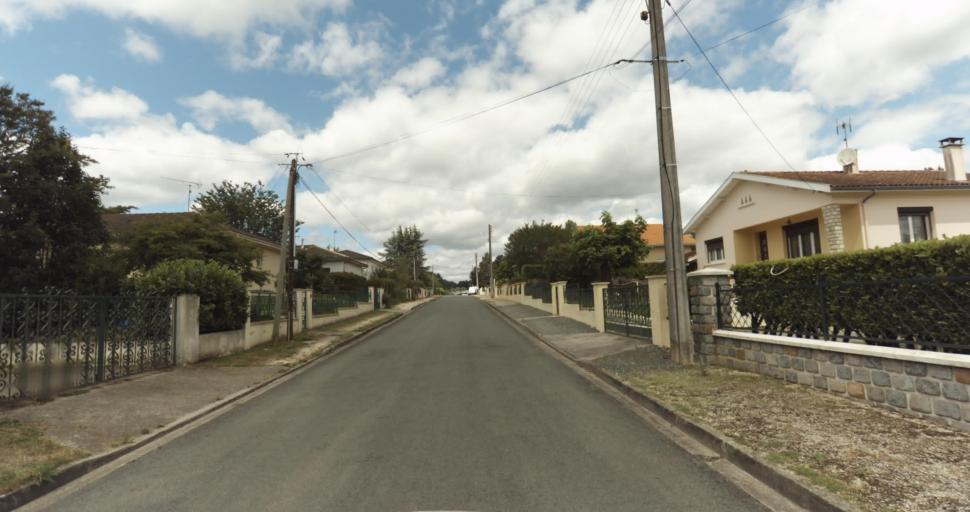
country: FR
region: Aquitaine
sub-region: Departement de la Gironde
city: Bazas
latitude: 44.4389
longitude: -0.2221
